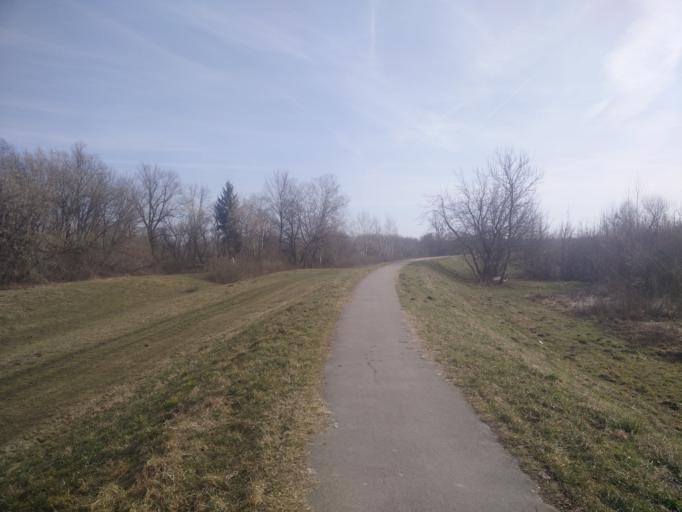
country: HR
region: Karlovacka
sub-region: Grad Karlovac
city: Karlovac
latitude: 45.5004
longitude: 15.5657
